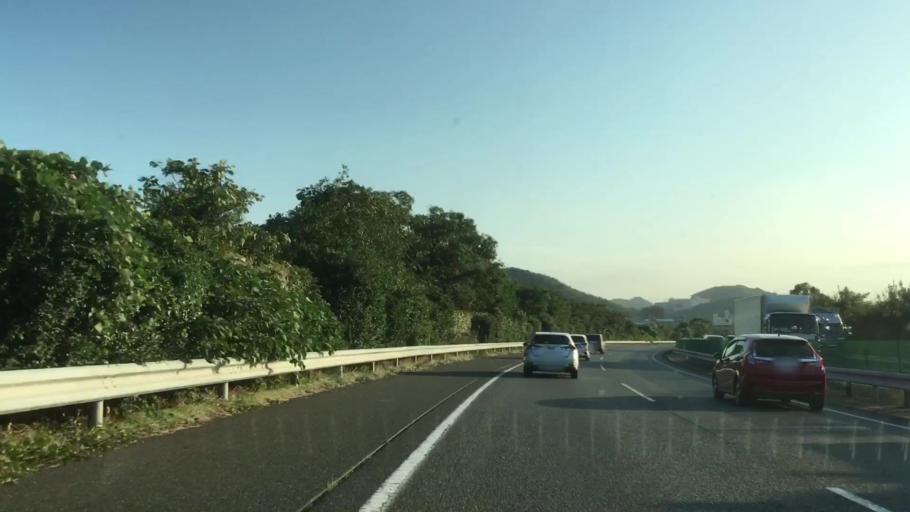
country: JP
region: Yamaguchi
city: Shimonoseki
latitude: 34.0169
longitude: 130.9575
